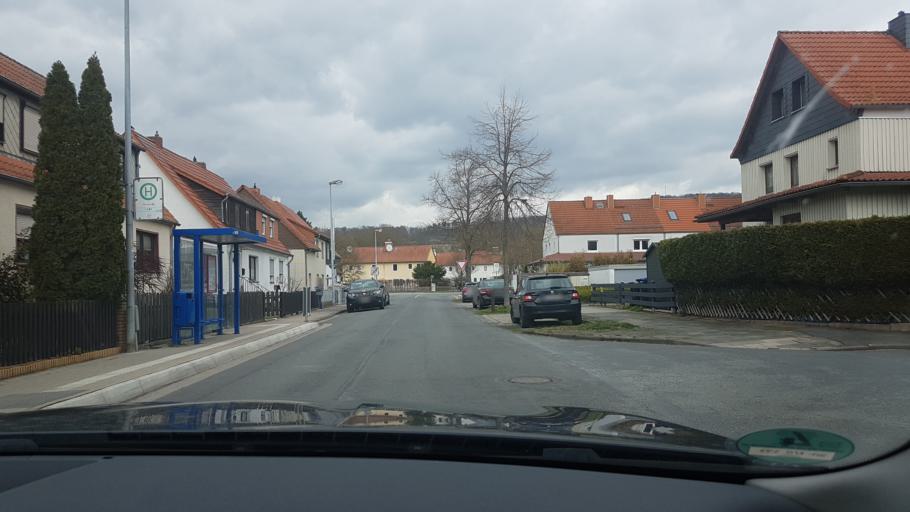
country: DE
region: Lower Saxony
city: Hameln
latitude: 52.1198
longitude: 9.3511
